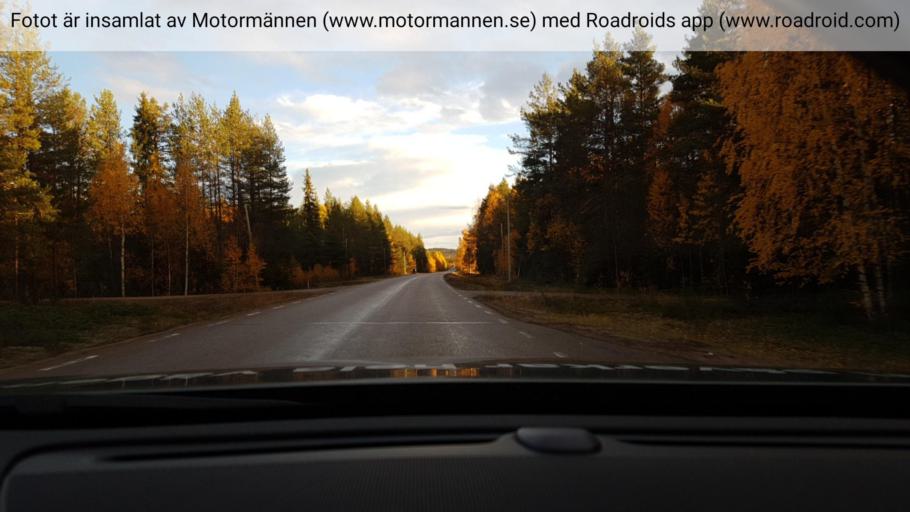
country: SE
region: Norrbotten
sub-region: Overkalix Kommun
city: OEverkalix
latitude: 66.6186
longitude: 22.7497
